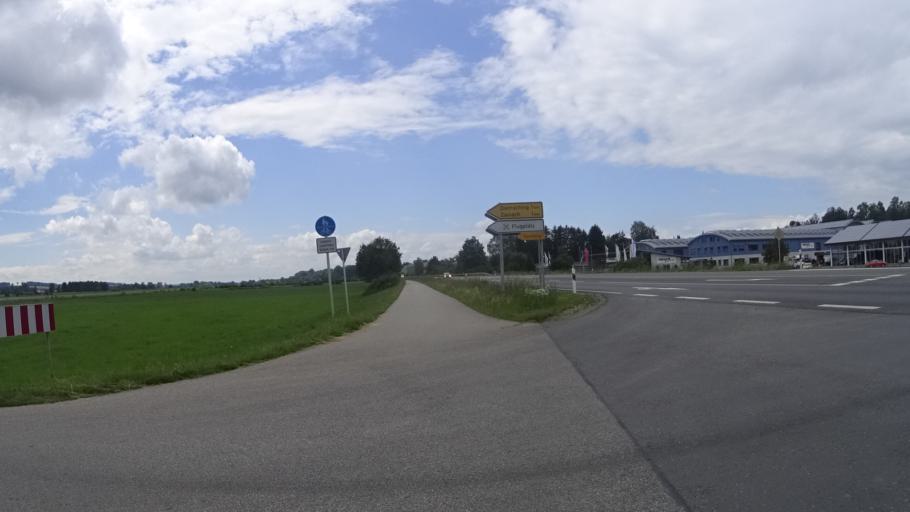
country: DE
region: Bavaria
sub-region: Lower Bavaria
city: Eggenfelden
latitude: 48.3976
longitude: 12.7308
